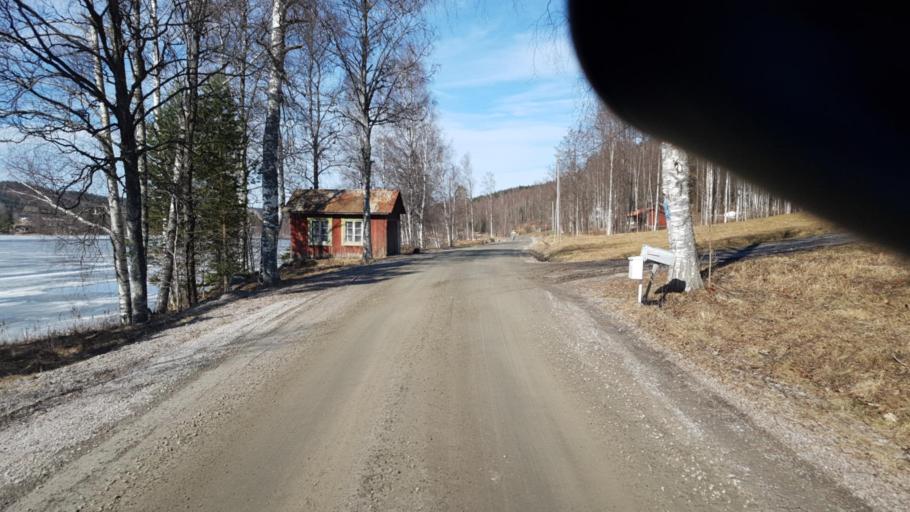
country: SE
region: Vaermland
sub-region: Arvika Kommun
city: Arvika
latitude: 59.7411
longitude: 12.8296
